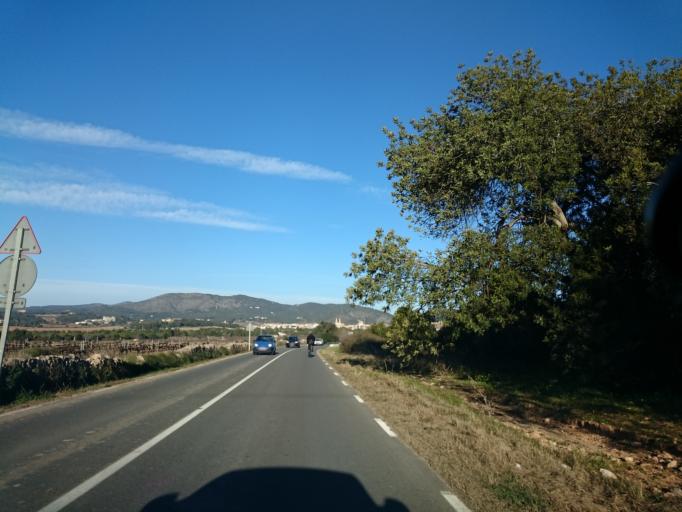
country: ES
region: Catalonia
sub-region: Provincia de Barcelona
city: Sitges
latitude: 41.2463
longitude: 1.7898
